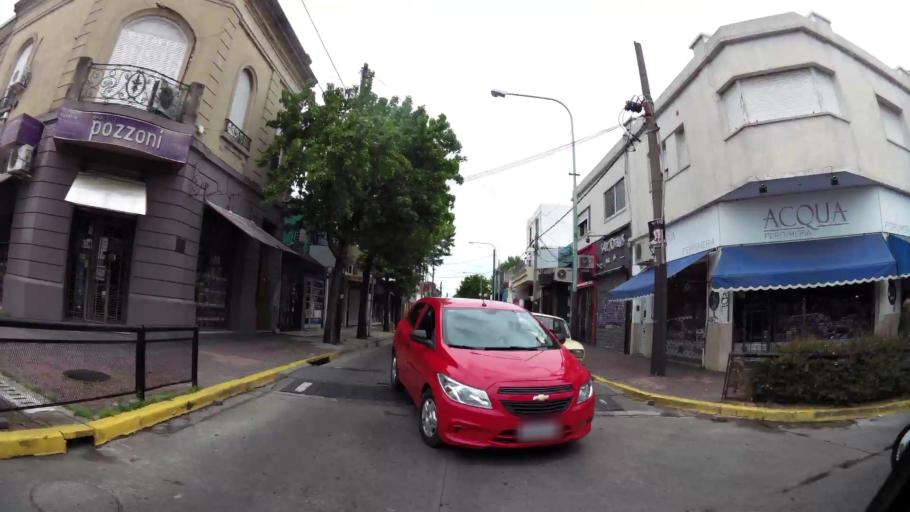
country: AR
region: Buenos Aires
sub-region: Partido de Quilmes
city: Quilmes
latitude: -34.7608
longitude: -58.2102
